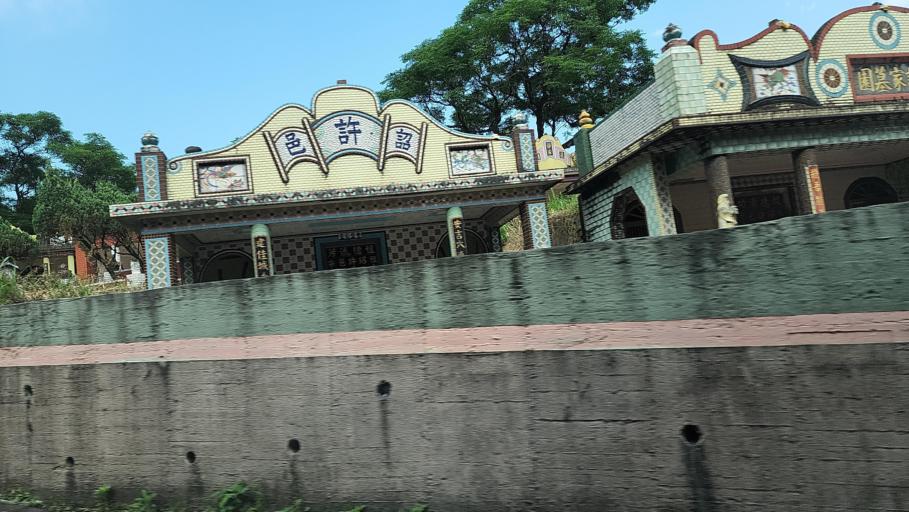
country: TW
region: Taiwan
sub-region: Keelung
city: Keelung
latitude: 25.2234
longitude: 121.6376
